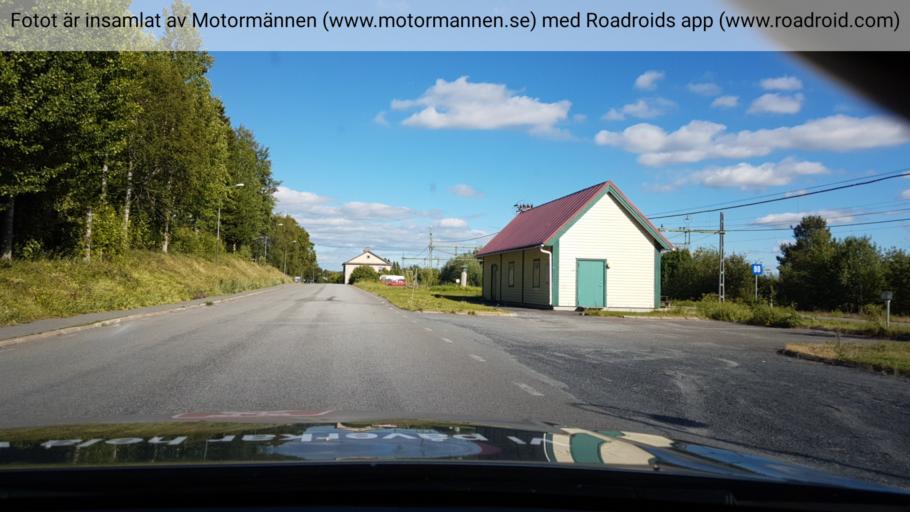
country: SE
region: Jaemtland
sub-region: Are Kommun
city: Jarpen
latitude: 63.3088
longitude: 13.6579
